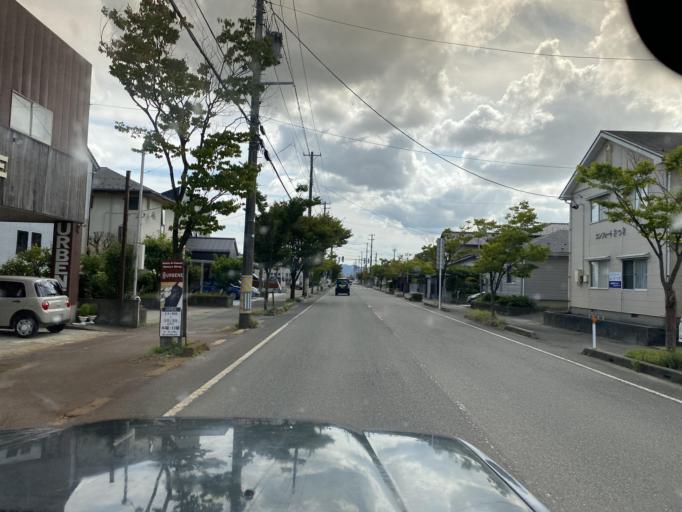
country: JP
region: Niigata
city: Niitsu-honcho
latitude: 37.8125
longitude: 139.1160
